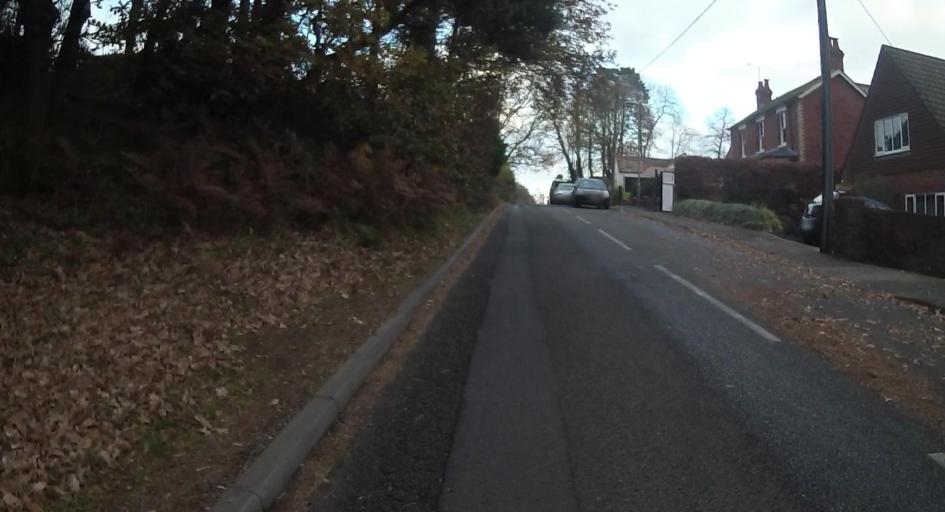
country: GB
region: England
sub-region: Bracknell Forest
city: Sandhurst
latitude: 51.3566
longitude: -0.7809
